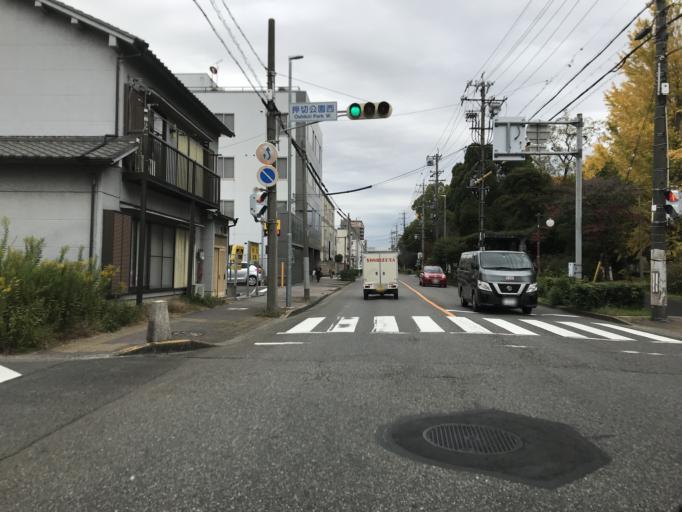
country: JP
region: Aichi
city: Nagoya-shi
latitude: 35.1919
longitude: 136.8839
